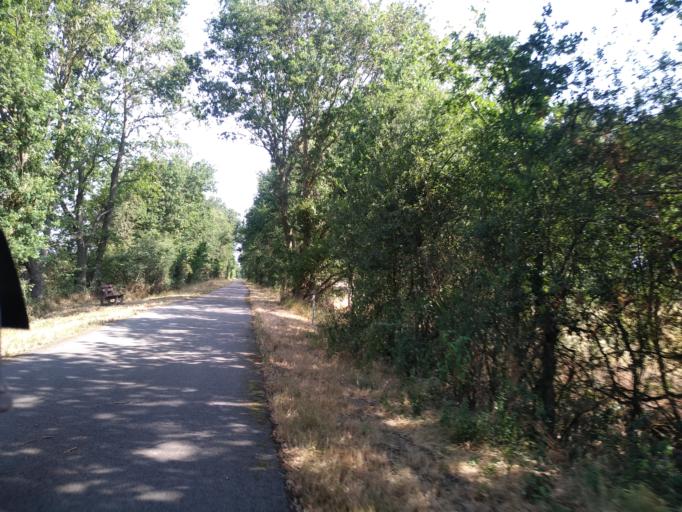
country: FR
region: Bourgogne
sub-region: Departement de Saone-et-Loire
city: Marcigny
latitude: 46.3252
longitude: 4.0284
